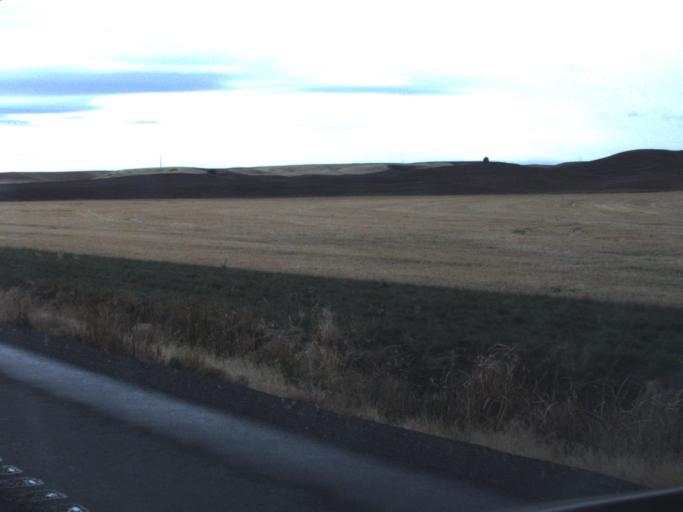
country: US
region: Washington
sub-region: Asotin County
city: Clarkston
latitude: 46.5128
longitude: -117.0803
